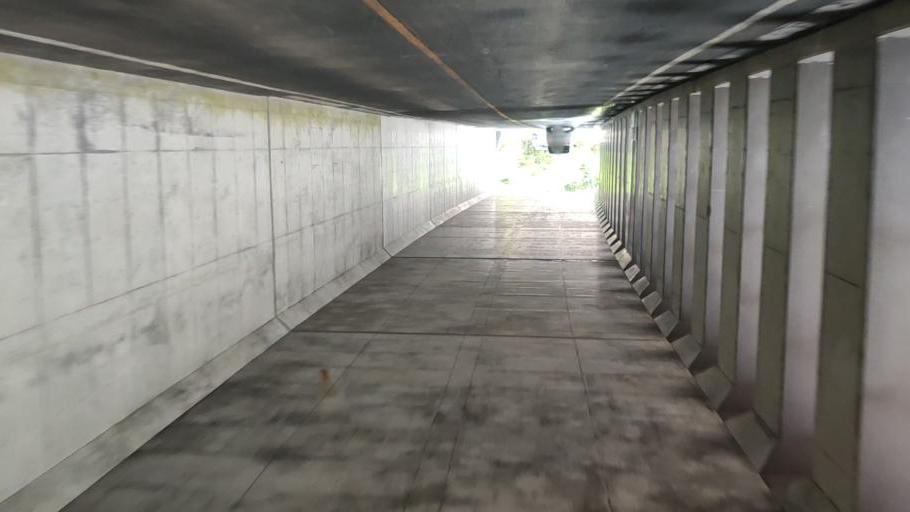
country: JP
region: Yamanashi
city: Fujikawaguchiko
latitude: 35.3906
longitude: 138.7174
